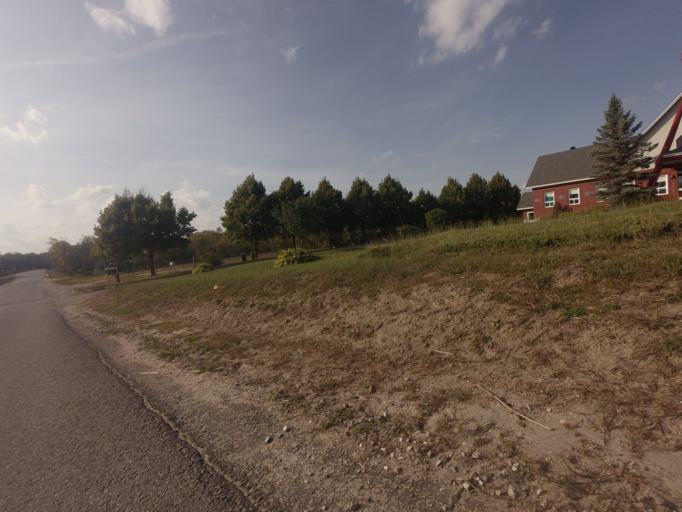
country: CA
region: Quebec
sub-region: Outaouais
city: Maniwaki
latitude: 46.3643
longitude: -75.9890
